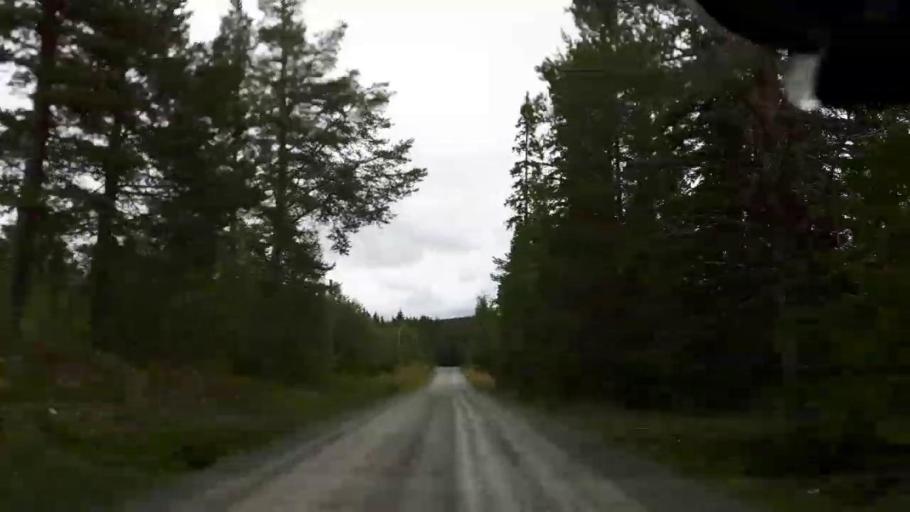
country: SE
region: Jaemtland
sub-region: Krokoms Kommun
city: Valla
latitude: 63.6935
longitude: 13.8676
